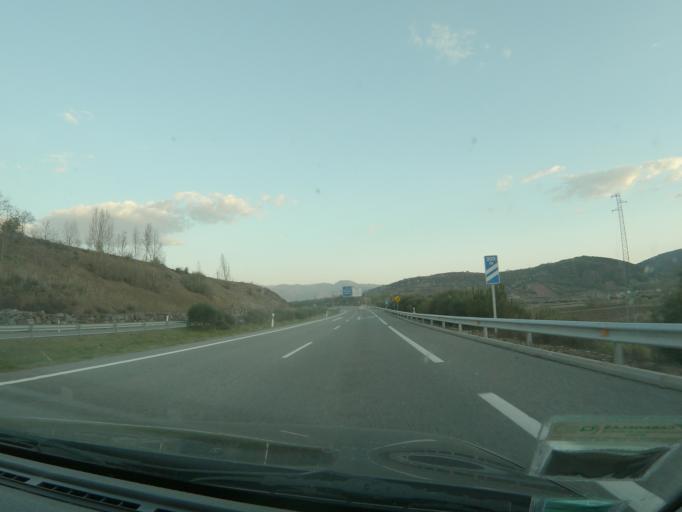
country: ES
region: Castille and Leon
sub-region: Provincia de Leon
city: Villafranca del Bierzo
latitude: 42.5887
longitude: -6.7935
